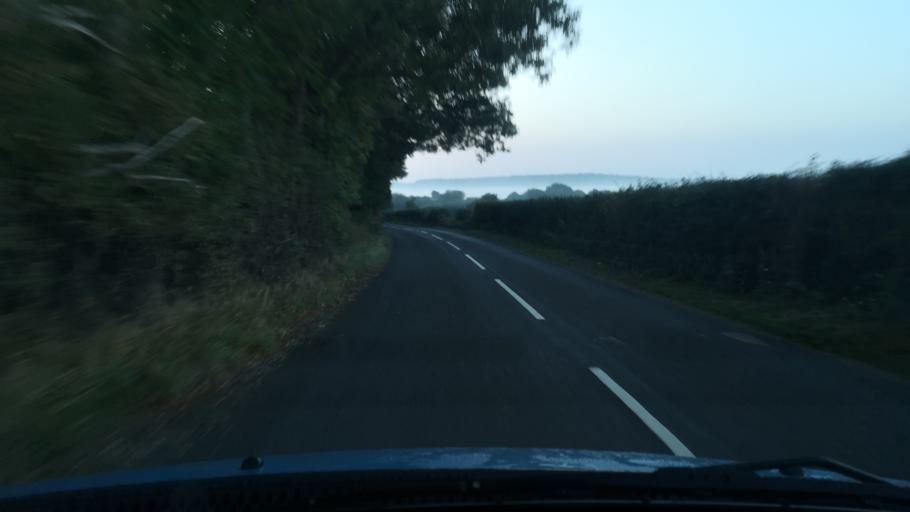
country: GB
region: England
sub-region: City and Borough of Wakefield
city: Darrington
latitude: 53.6600
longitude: -1.2827
